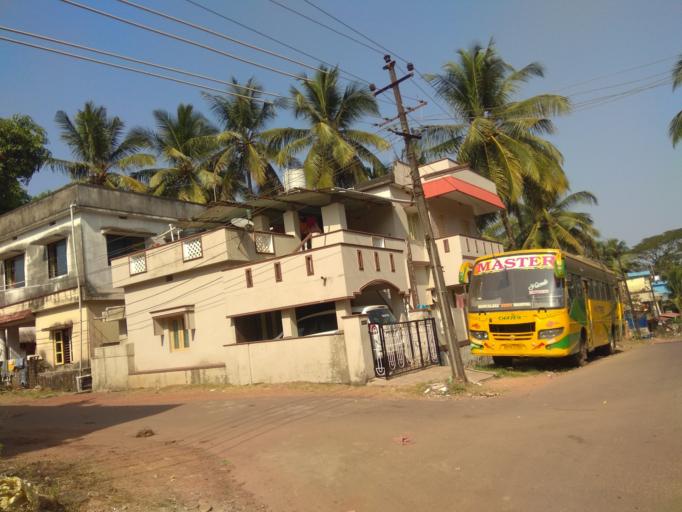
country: IN
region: Karnataka
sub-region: Dakshina Kannada
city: Mangalore
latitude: 12.9411
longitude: 74.8530
